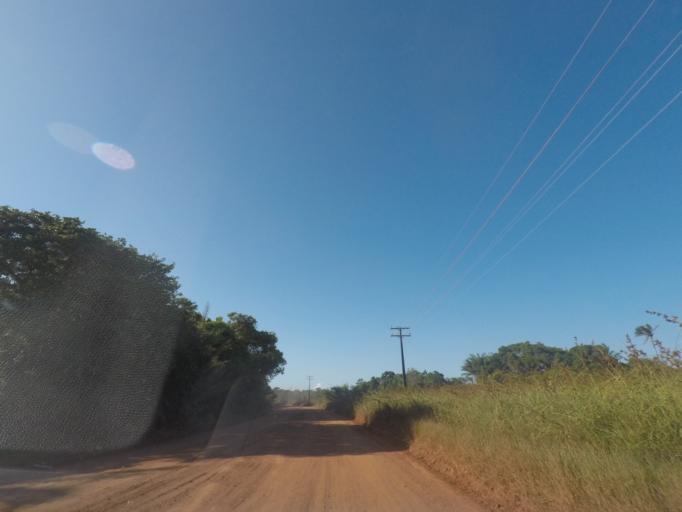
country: BR
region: Bahia
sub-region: Camamu
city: Camamu
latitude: -13.9475
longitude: -38.9456
